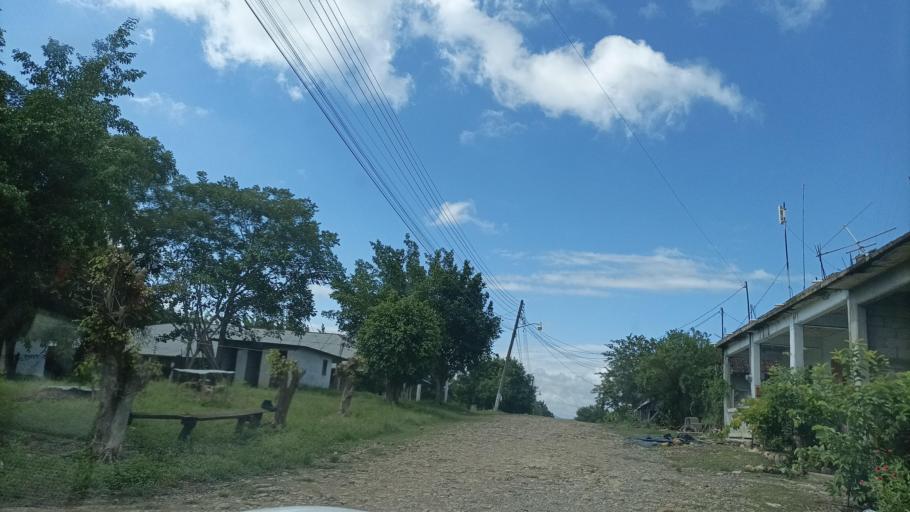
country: MX
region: Veracruz
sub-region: Tantoyuca
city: El Lindero
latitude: 21.1946
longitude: -98.1441
